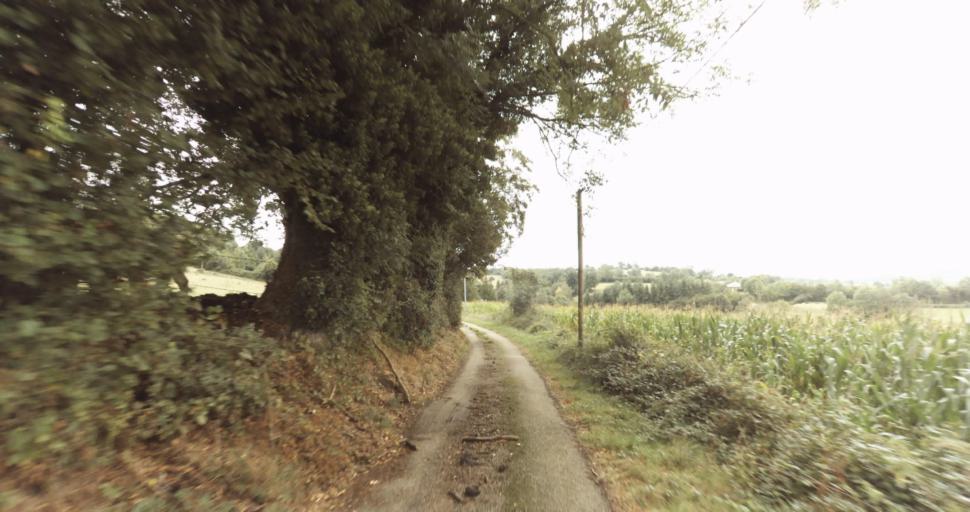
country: FR
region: Lower Normandy
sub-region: Departement de l'Orne
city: Vimoutiers
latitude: 48.8985
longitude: 0.1921
